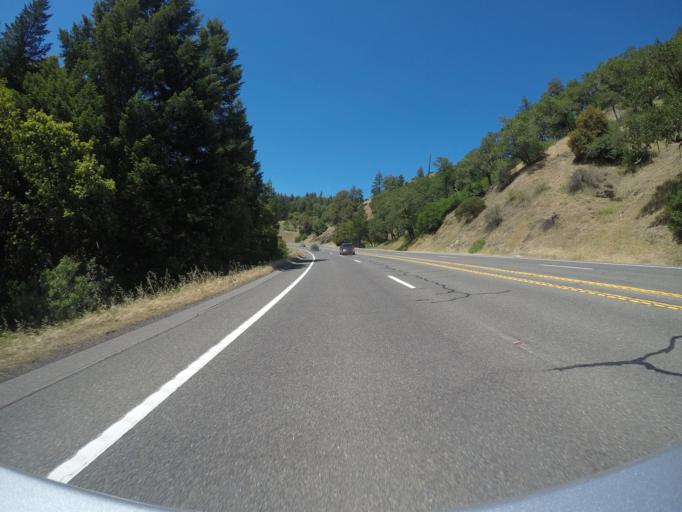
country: US
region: California
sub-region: Mendocino County
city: Laytonville
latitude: 39.6134
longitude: -123.4588
